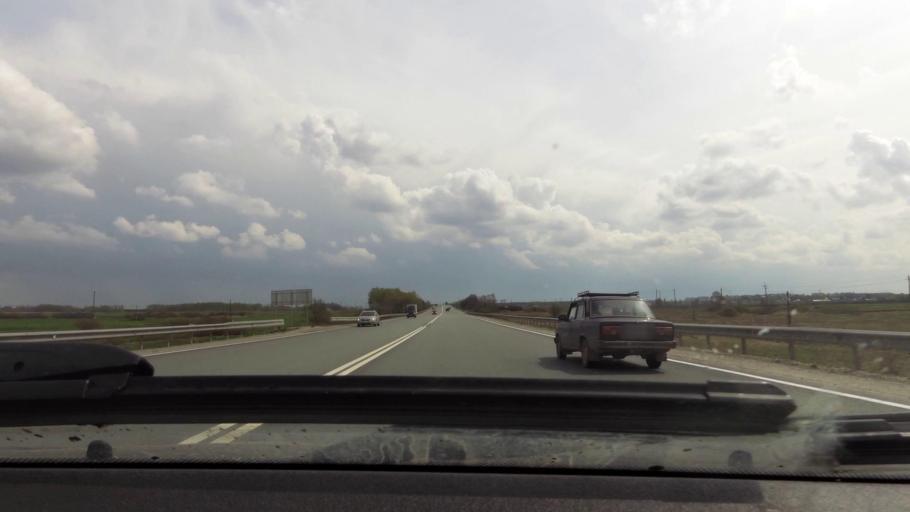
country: RU
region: Rjazan
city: Bagramovo
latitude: 54.7417
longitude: 39.4418
